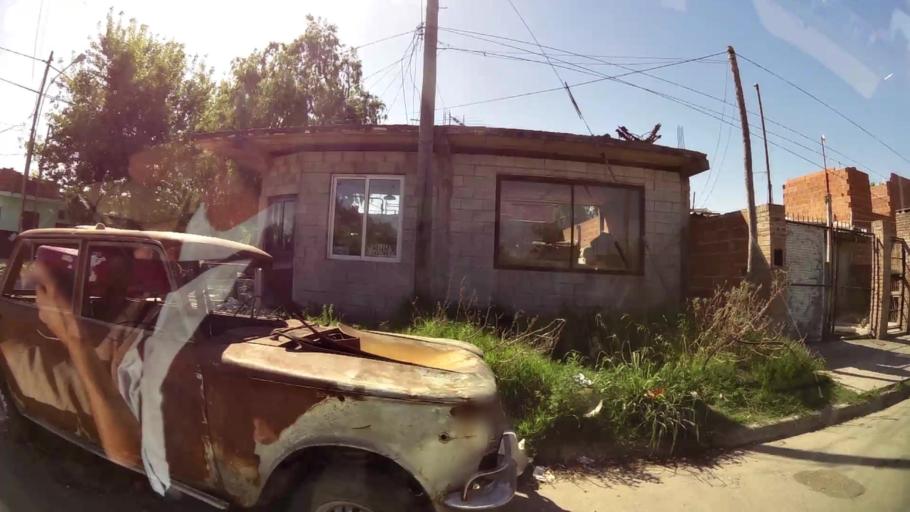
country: AR
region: Buenos Aires
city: Hurlingham
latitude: -34.5392
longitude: -58.5939
